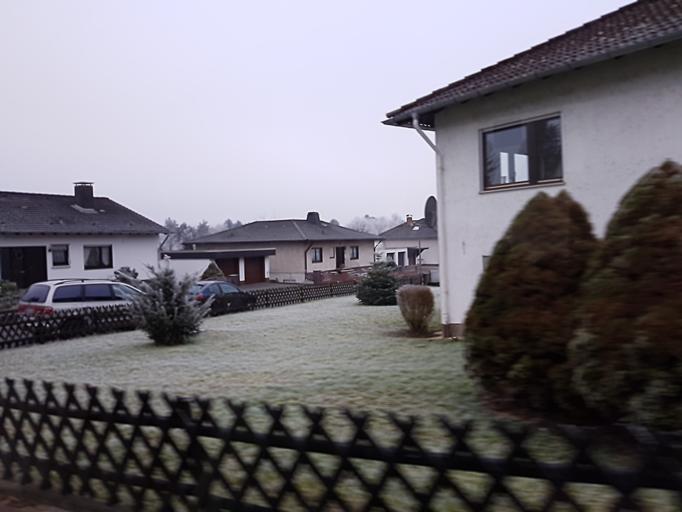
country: DE
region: Hesse
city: Niederbiel
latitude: 50.5548
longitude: 8.4031
